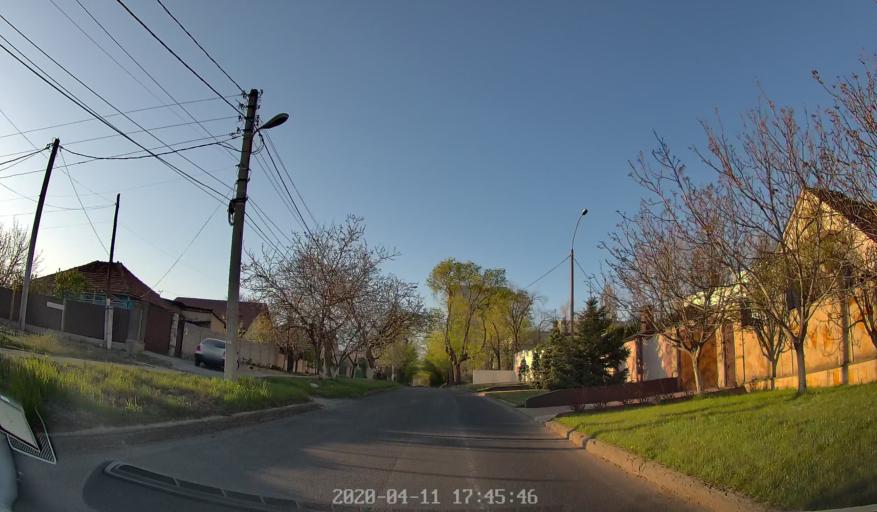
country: MD
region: Chisinau
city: Chisinau
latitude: 46.9876
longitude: 28.8220
